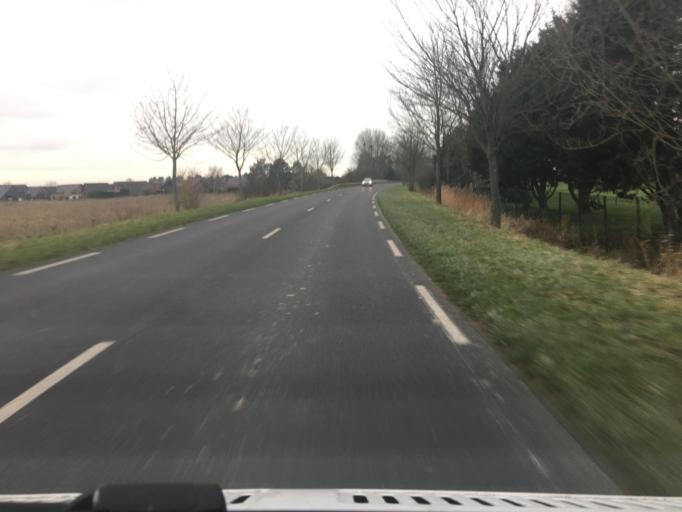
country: FR
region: Lower Normandy
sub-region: Departement du Calvados
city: Cabourg
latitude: 49.2748
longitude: -0.1271
